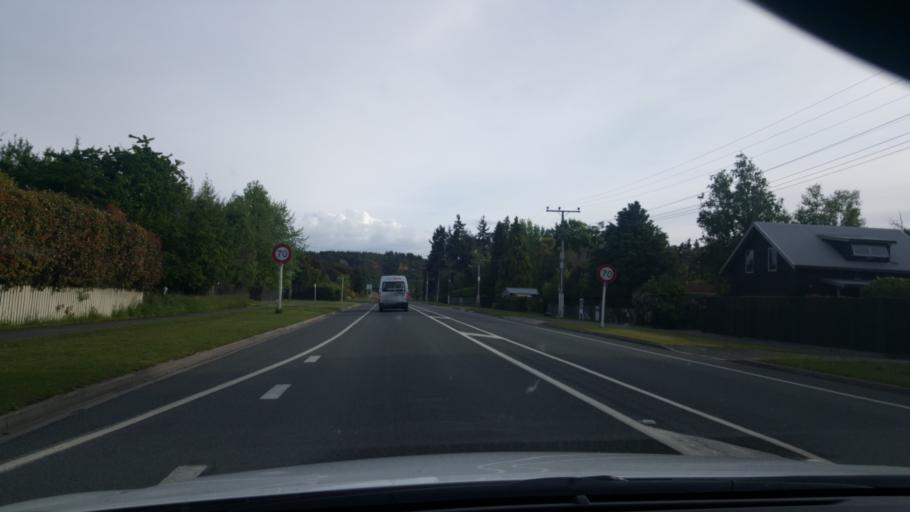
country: NZ
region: Waikato
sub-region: Taupo District
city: Taupo
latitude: -38.7916
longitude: 176.0761
